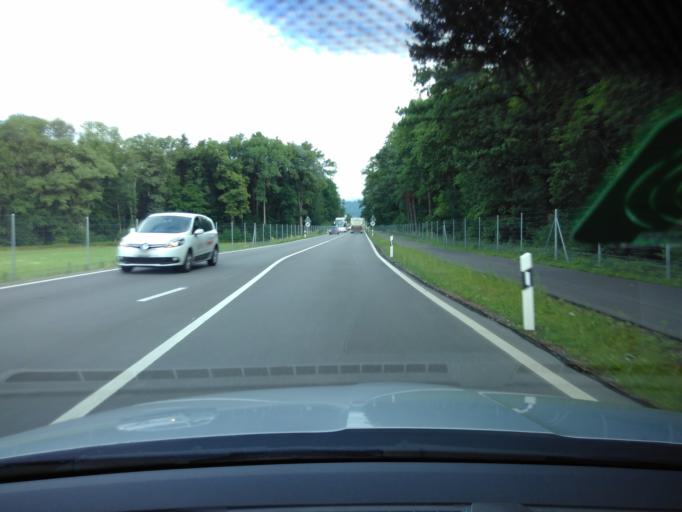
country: CH
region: Zurich
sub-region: Bezirk Dielsdorf
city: Regensdorf
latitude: 47.4327
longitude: 8.4822
